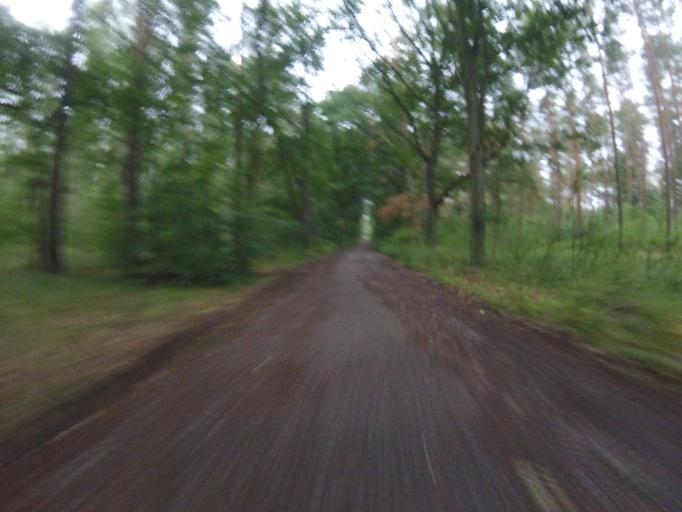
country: DE
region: Brandenburg
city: Bestensee
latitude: 52.2207
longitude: 13.7067
